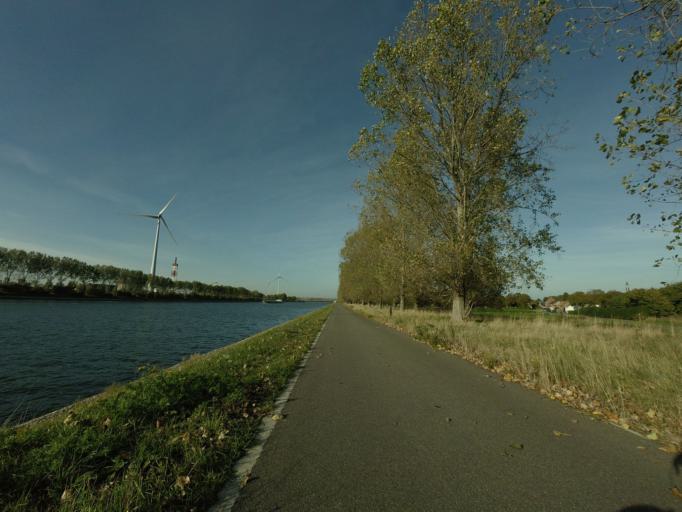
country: NL
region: North Brabant
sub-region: Gemeente Woensdrecht
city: Woensdrecht
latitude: 51.3570
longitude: 4.3019
